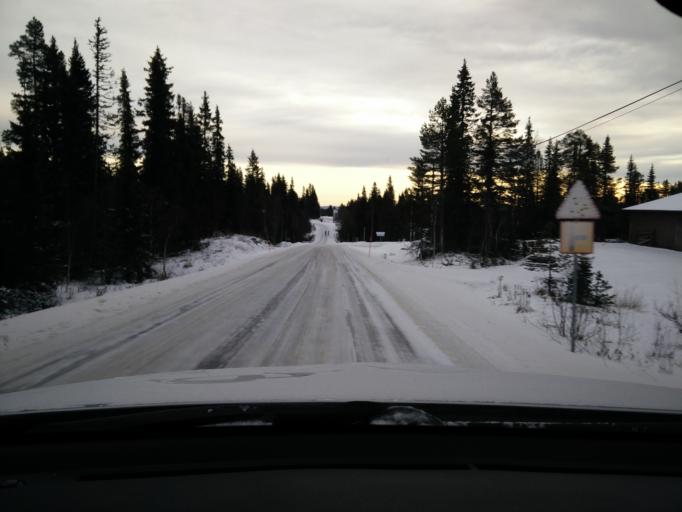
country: SE
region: Jaemtland
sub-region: Bergs Kommun
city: Hoverberg
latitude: 62.4798
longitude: 14.1254
